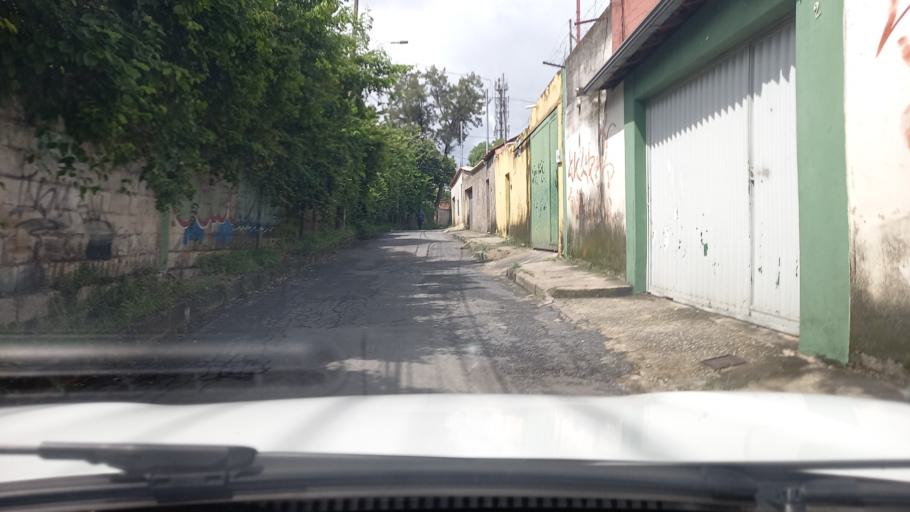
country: BR
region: Minas Gerais
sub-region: Contagem
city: Contagem
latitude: -19.8978
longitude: -44.0229
